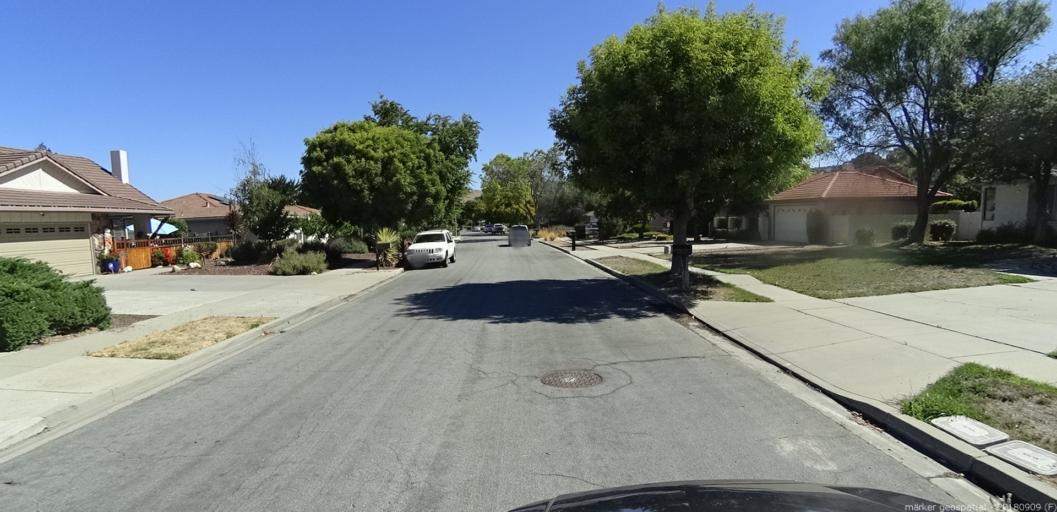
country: US
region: California
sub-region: Monterey County
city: Salinas
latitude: 36.5959
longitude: -121.7024
